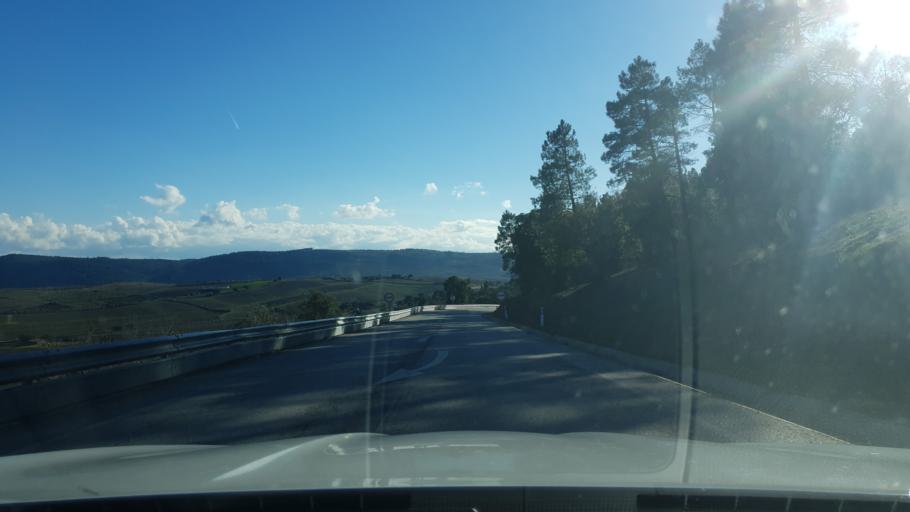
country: PT
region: Braganca
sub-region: Freixo de Espada A Cinta
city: Freixo de Espada a Cinta
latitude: 41.1014
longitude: -6.8295
